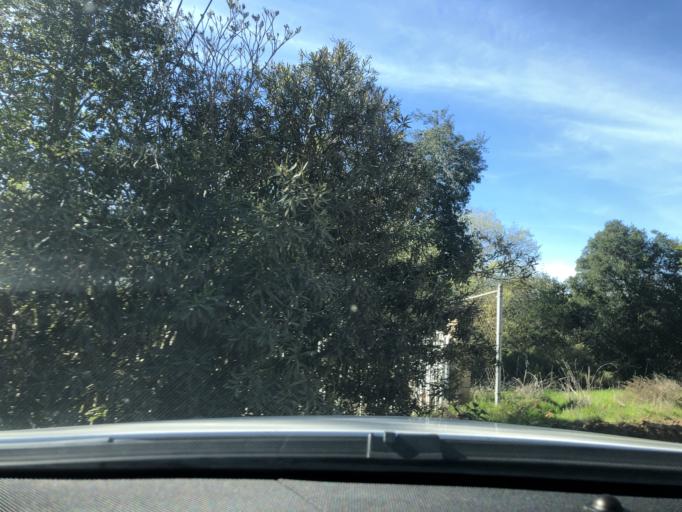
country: US
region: California
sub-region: San Diego County
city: Escondido
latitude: 33.0869
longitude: -117.0881
